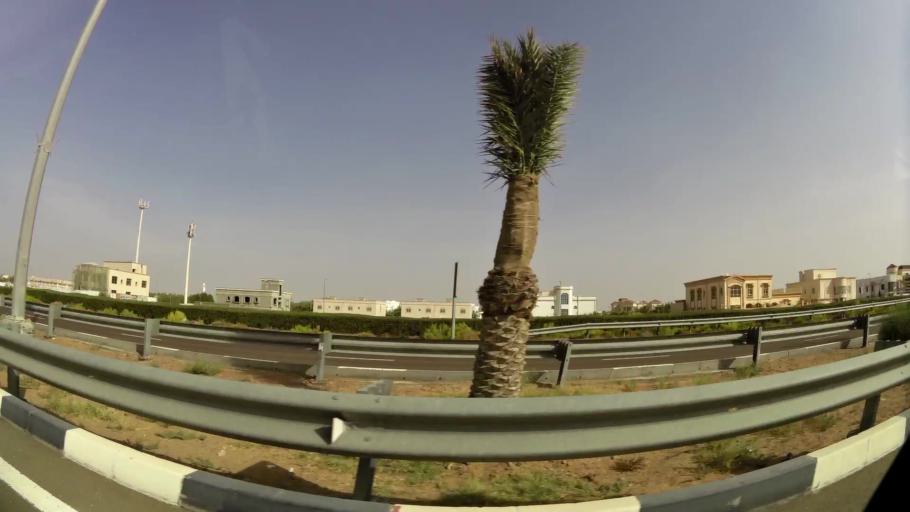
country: AE
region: Abu Dhabi
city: Al Ain
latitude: 24.2211
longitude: 55.6456
